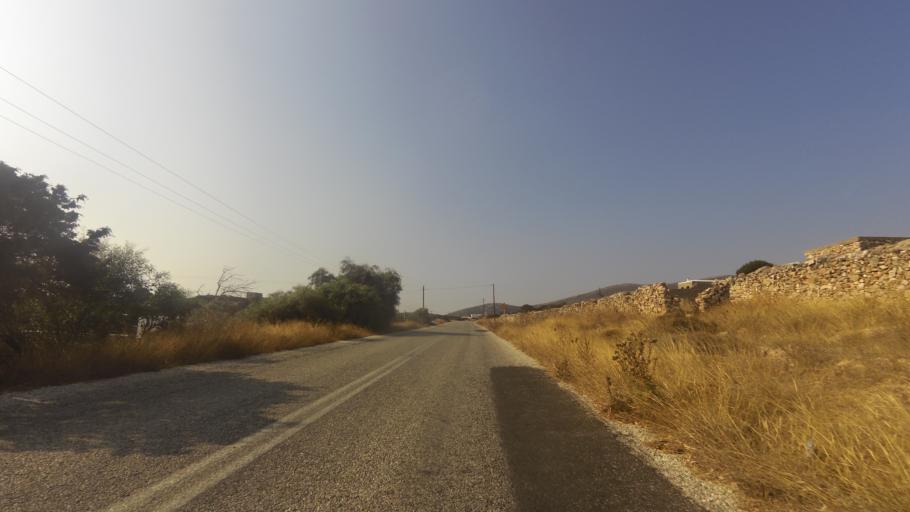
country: GR
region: South Aegean
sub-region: Nomos Kykladon
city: Antiparos
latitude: 37.0035
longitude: 25.0730
